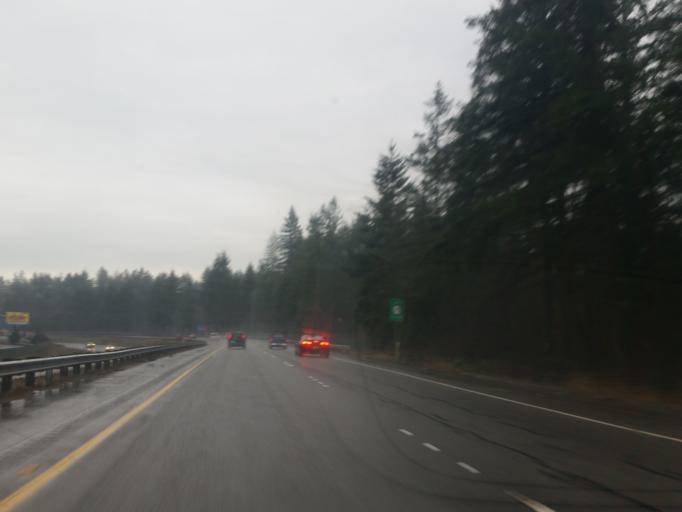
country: US
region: Washington
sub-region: Snohomish County
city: Maltby
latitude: 47.7947
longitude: -122.1216
